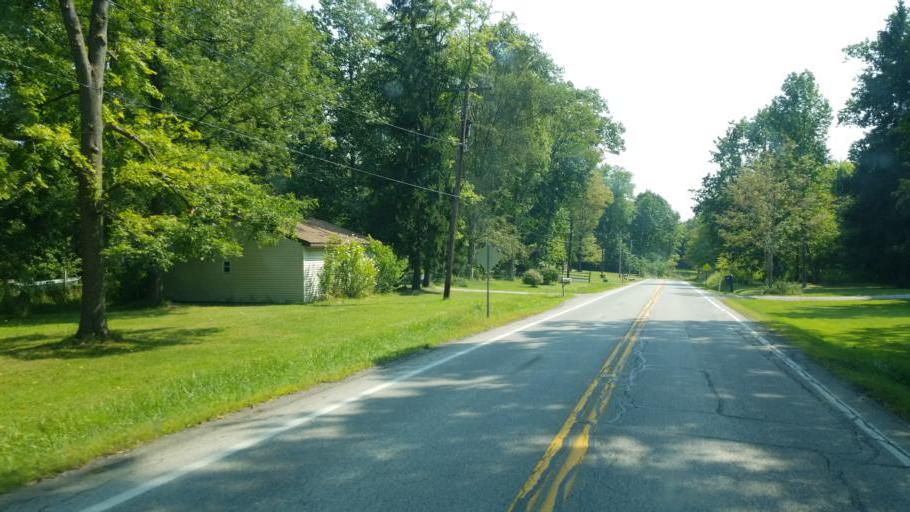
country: US
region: Ohio
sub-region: Ashtabula County
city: Orwell
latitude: 41.5427
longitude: -80.9437
